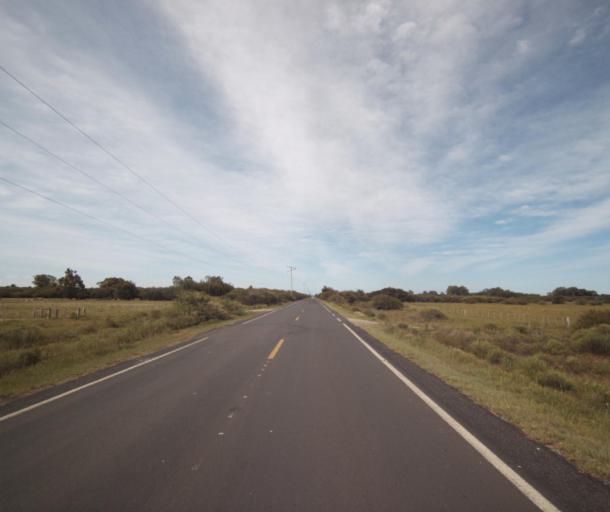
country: BR
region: Rio Grande do Sul
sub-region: Rio Grande
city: Rio Grande
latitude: -31.9199
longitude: -51.9472
